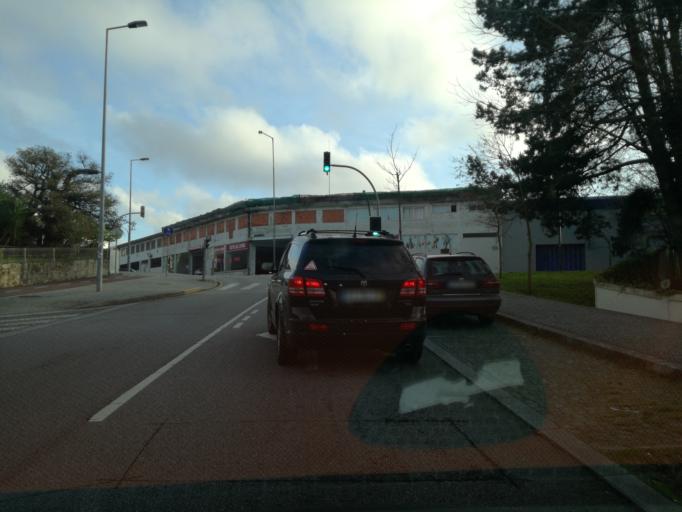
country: PT
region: Porto
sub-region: Matosinhos
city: Senhora da Hora
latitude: 41.1700
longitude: -8.6321
